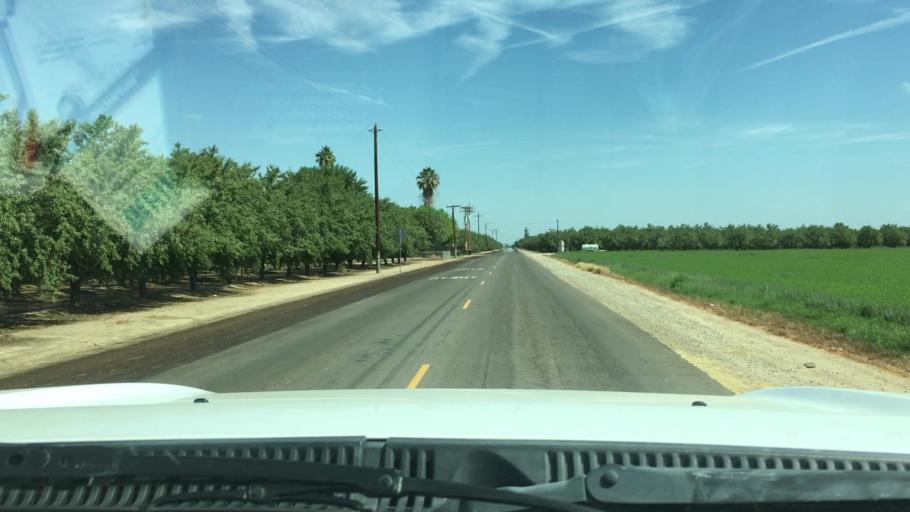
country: US
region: California
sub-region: Kern County
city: Shafter
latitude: 35.5020
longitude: -119.3502
